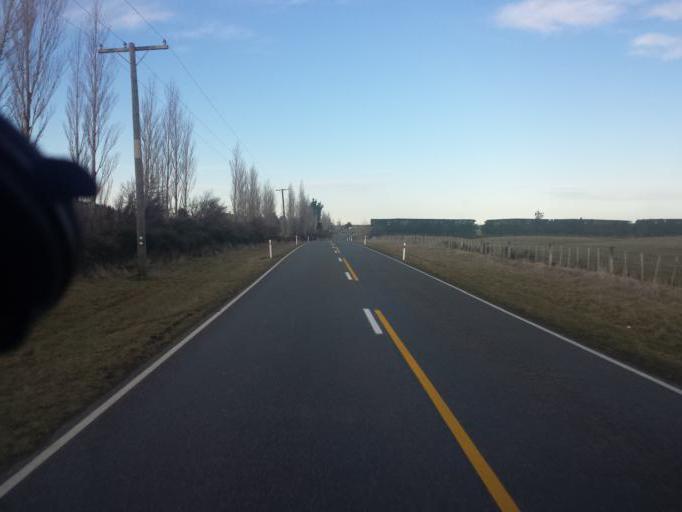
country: NZ
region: Canterbury
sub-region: Ashburton District
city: Methven
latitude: -43.5190
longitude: 171.8184
